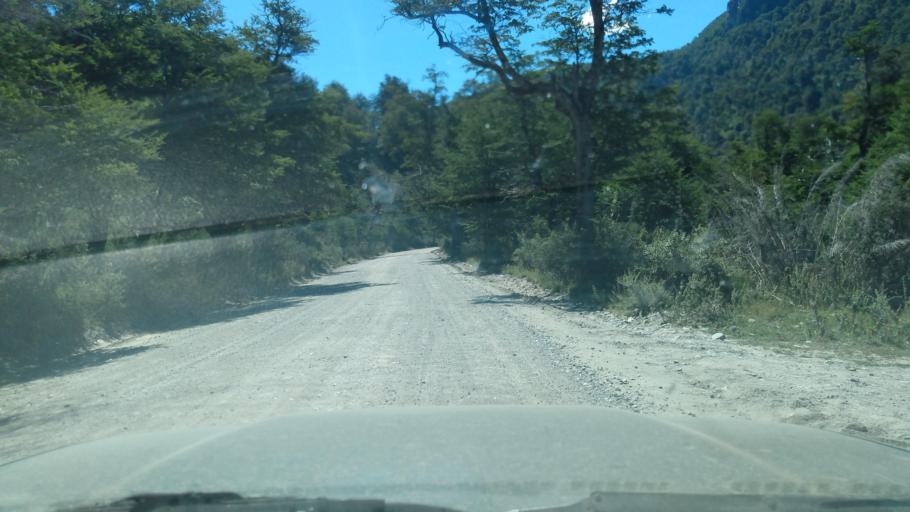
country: AR
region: Neuquen
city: Villa La Angostura
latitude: -40.6081
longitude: -71.6139
